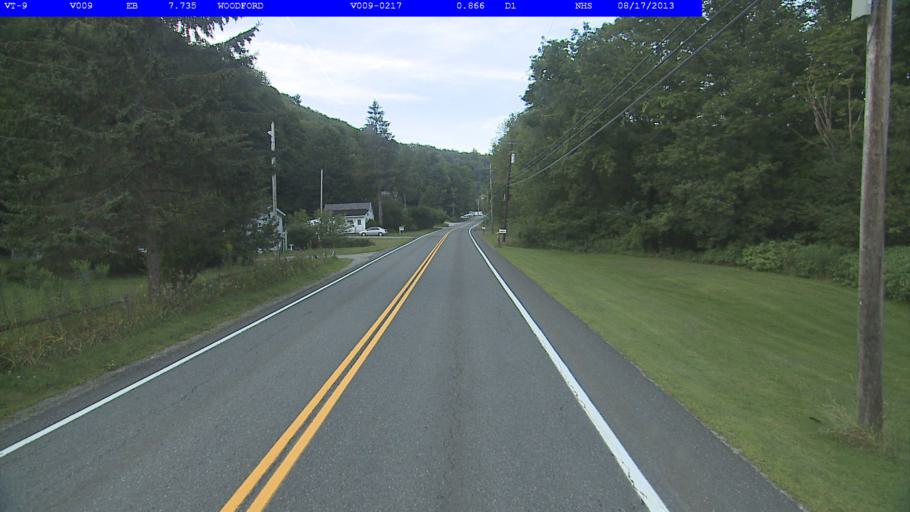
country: US
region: Vermont
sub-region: Bennington County
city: Bennington
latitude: 42.8922
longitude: -73.1383
